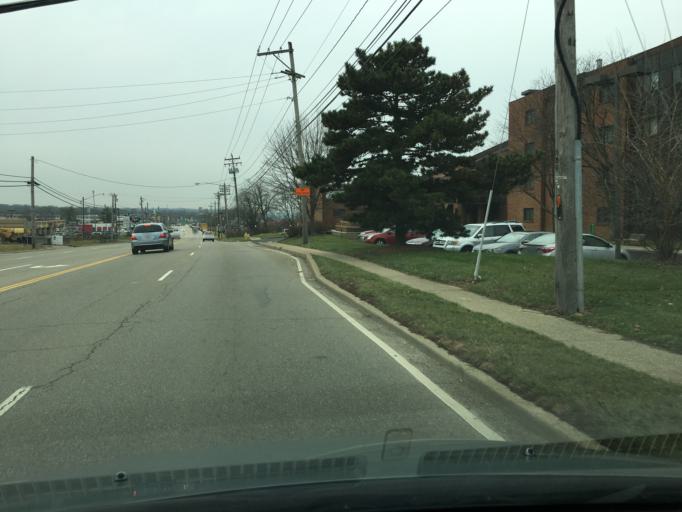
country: US
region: Ohio
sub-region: Hamilton County
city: Sharonville
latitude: 39.2955
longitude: -84.3924
